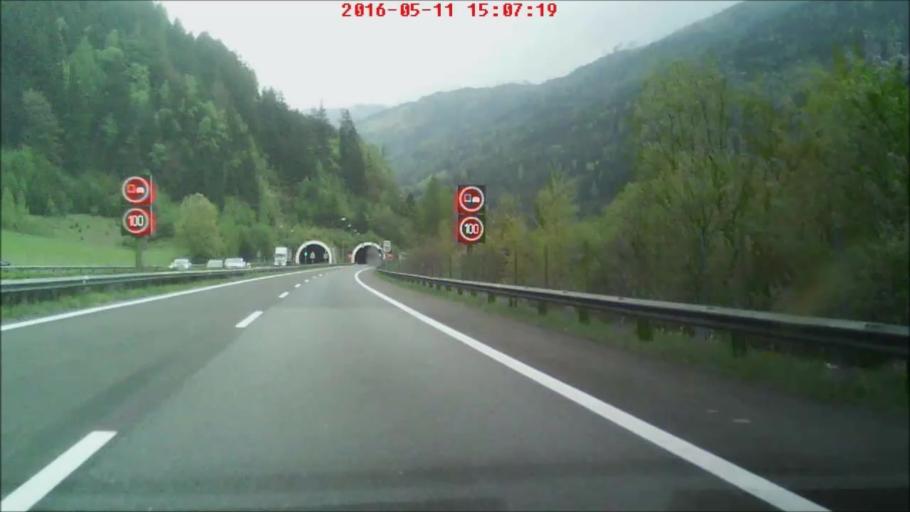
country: AT
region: Styria
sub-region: Politischer Bezirk Leoben
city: Wald am Schoberpass
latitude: 47.4346
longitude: 14.7018
